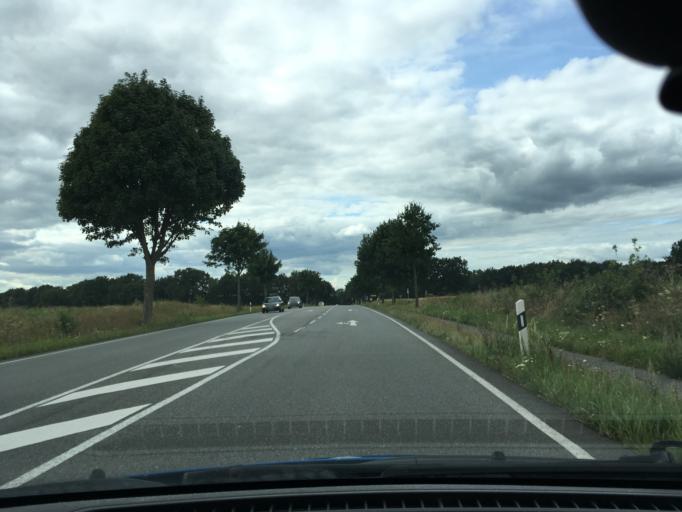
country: DE
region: Lower Saxony
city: Neu Wulmstorf
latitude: 53.4398
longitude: 9.7654
